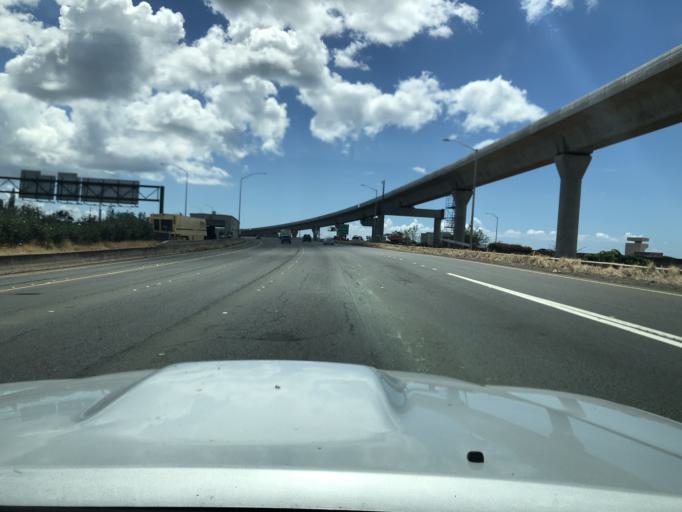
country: US
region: Hawaii
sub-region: Honolulu County
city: Hickam Field
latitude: 21.3425
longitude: -157.9322
